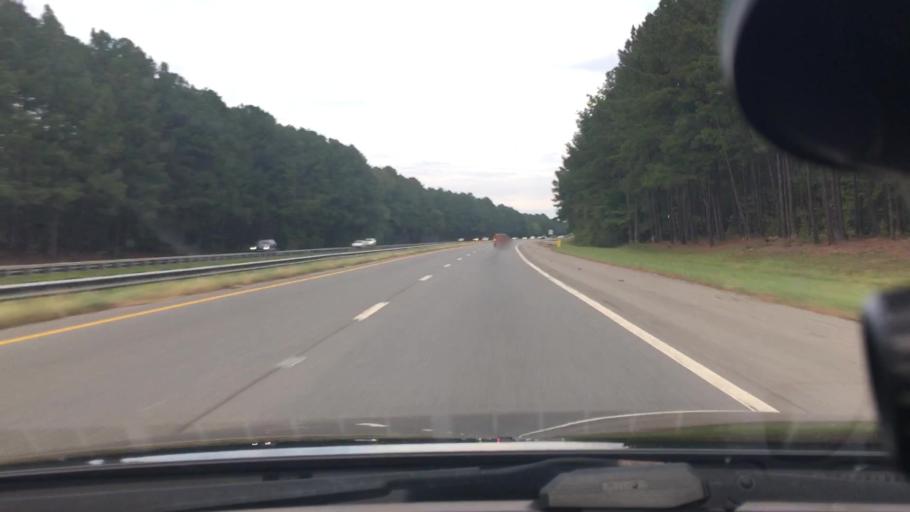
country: US
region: North Carolina
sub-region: Chatham County
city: Farmville
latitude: 35.5676
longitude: -79.1475
